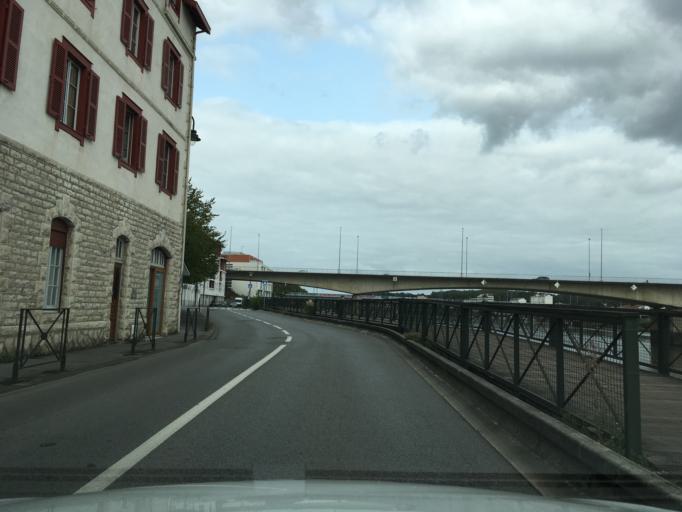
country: FR
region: Aquitaine
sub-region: Departement des Pyrenees-Atlantiques
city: Bayonne
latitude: 43.4861
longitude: -1.4610
